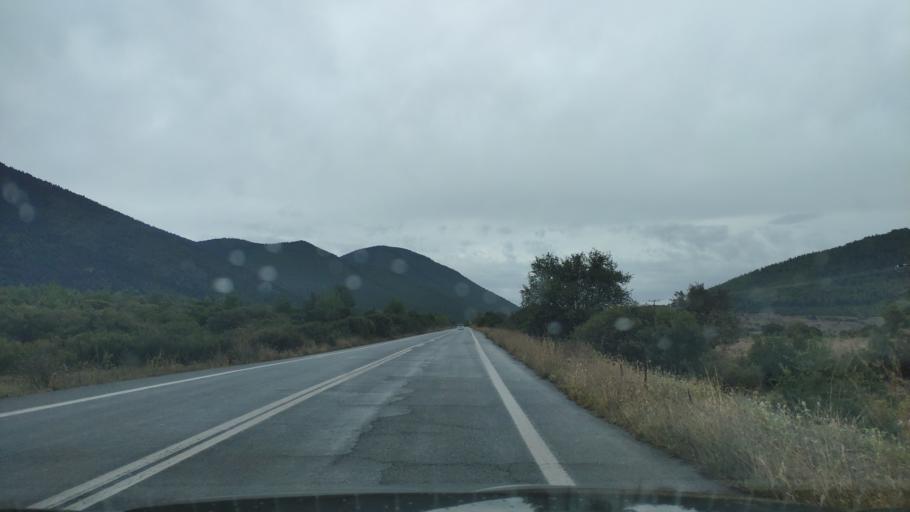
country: GR
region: Peloponnese
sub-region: Nomos Arkadias
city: Tripoli
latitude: 37.6576
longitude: 22.3112
